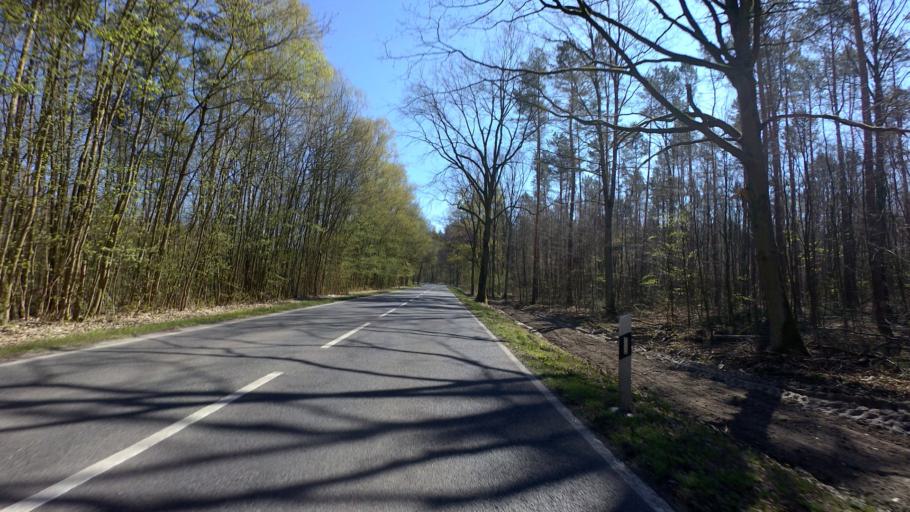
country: DE
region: Brandenburg
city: Schulzendorf
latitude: 52.3408
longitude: 13.5728
